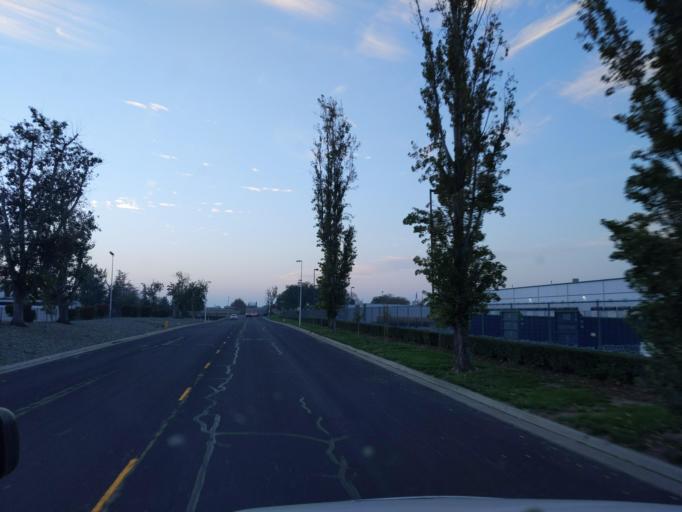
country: US
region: California
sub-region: San Joaquin County
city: Lathrop
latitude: 37.7984
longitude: -121.2963
